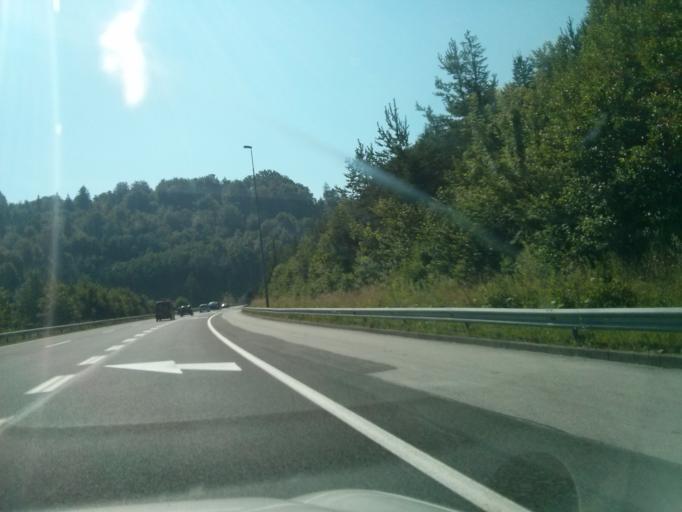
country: SI
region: Skofljica
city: Lavrica
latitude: 46.0118
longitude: 14.5616
